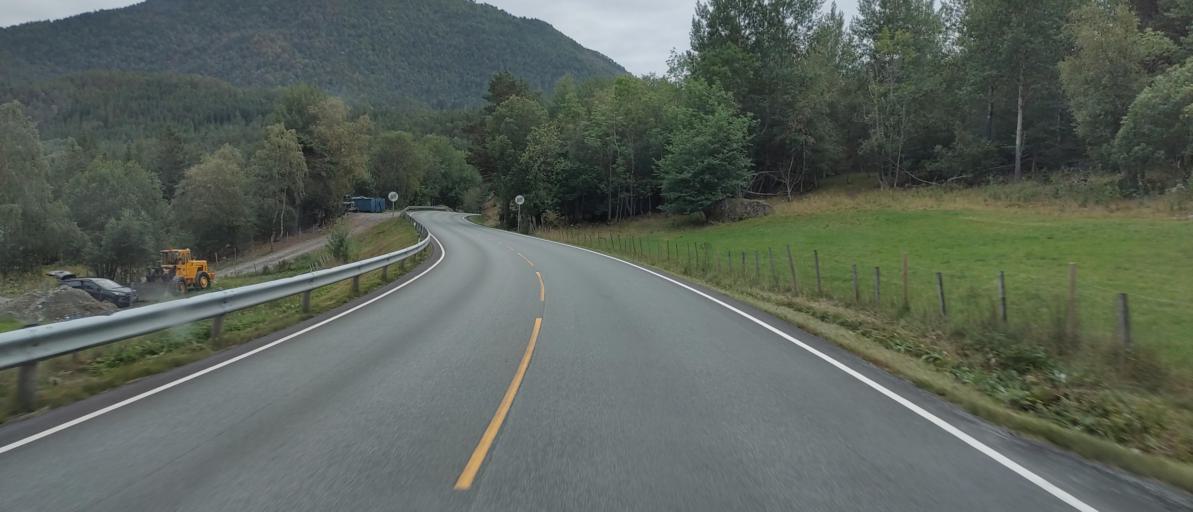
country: NO
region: More og Romsdal
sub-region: Rauma
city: Andalsnes
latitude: 62.5796
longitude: 7.5502
